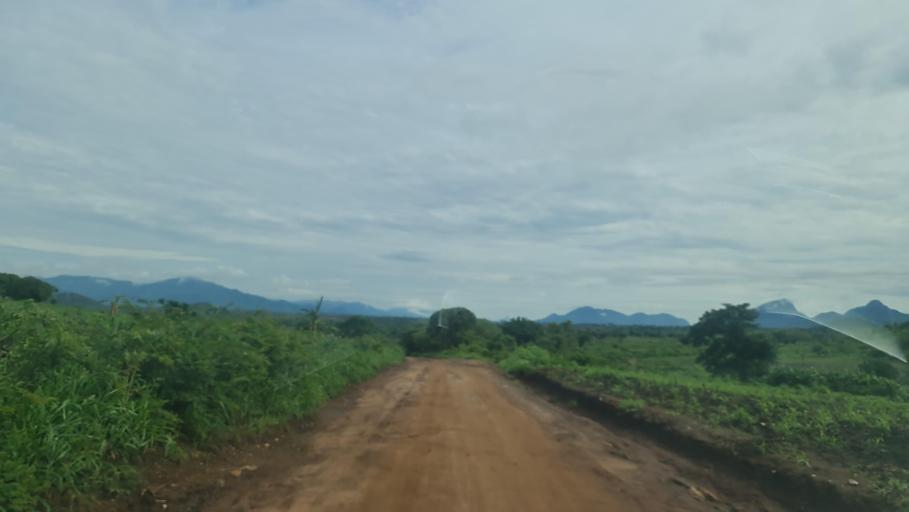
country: MZ
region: Nampula
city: Mutuali
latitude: -15.3052
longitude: 36.7592
